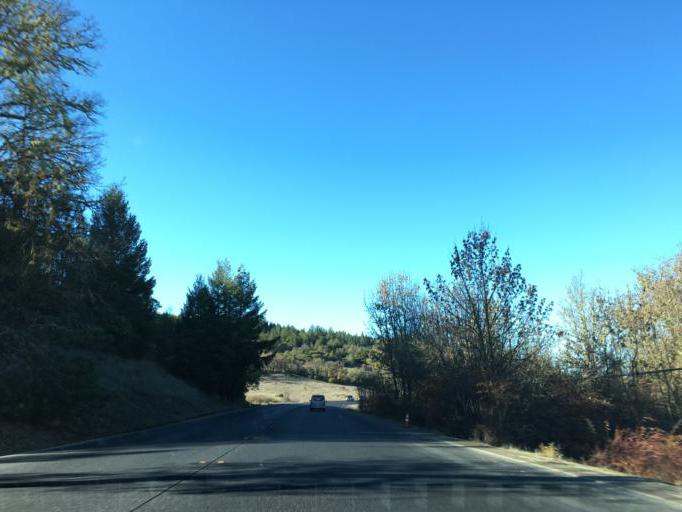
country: US
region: California
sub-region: Mendocino County
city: Laytonville
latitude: 39.6324
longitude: -123.4657
